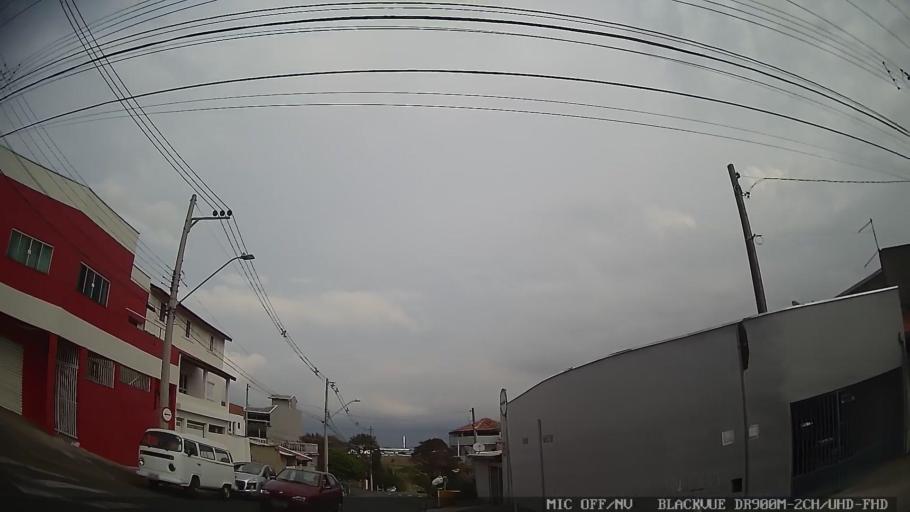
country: BR
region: Sao Paulo
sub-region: Indaiatuba
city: Indaiatuba
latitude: -23.1293
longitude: -47.2447
